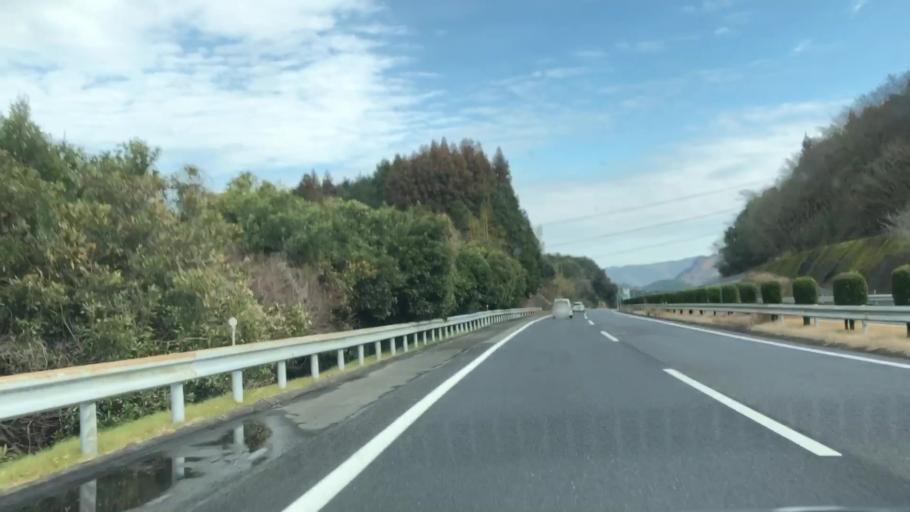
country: JP
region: Saga Prefecture
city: Takeocho-takeo
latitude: 33.1591
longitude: 130.0104
